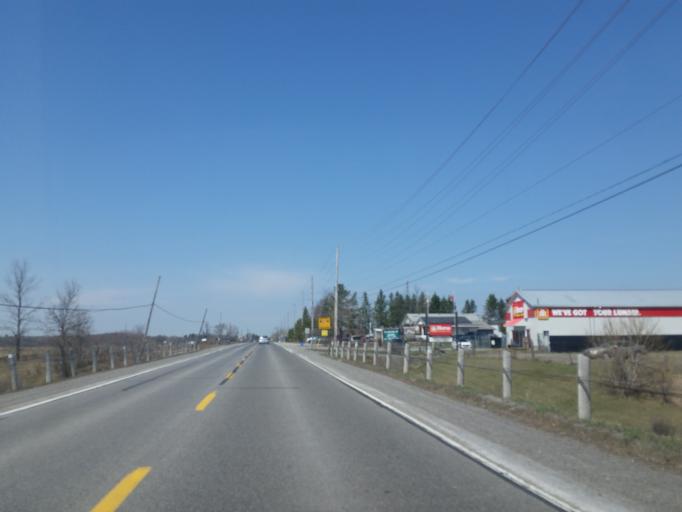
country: CA
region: Ontario
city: Bells Corners
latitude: 45.4590
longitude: -76.0706
